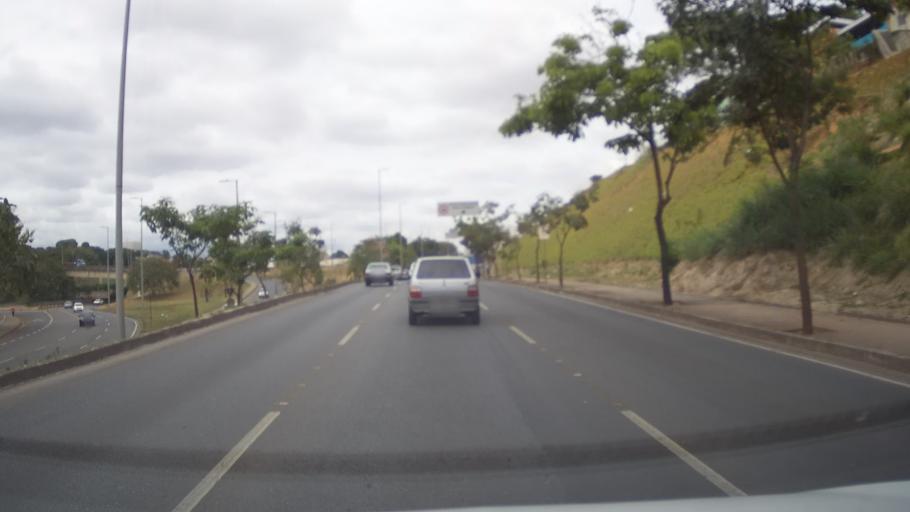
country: BR
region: Minas Gerais
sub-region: Belo Horizonte
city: Belo Horizonte
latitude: -19.8586
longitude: -43.9244
